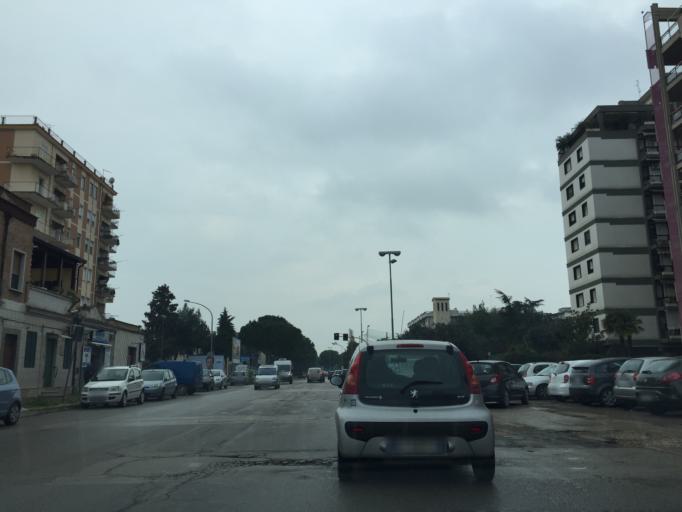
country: IT
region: Apulia
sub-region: Provincia di Foggia
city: Foggia
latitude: 41.4589
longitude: 15.5347
